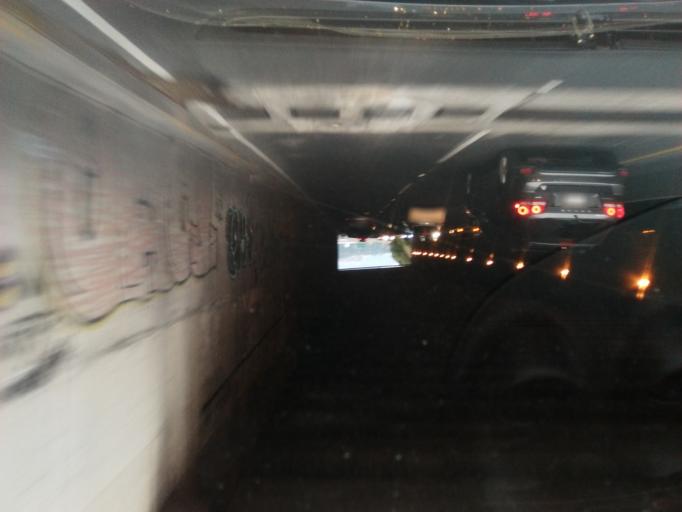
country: MX
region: Mexico City
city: Col. Bosques de las Lomas
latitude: 19.3577
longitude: -99.2605
